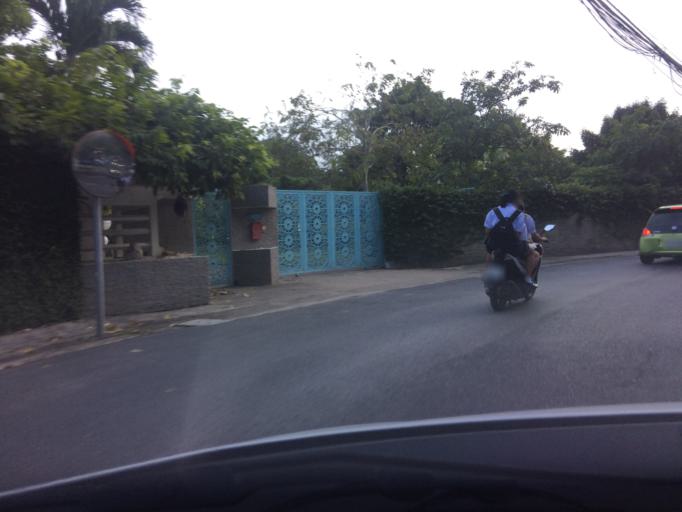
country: TH
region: Phuket
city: Ban Talat Yai
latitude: 7.8730
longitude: 98.3968
